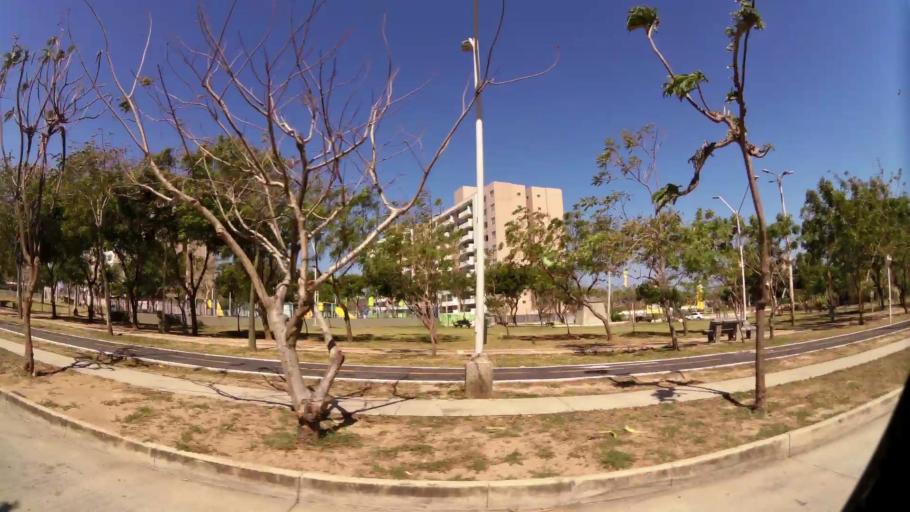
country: CO
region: Atlantico
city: Barranquilla
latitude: 11.0198
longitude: -74.8235
